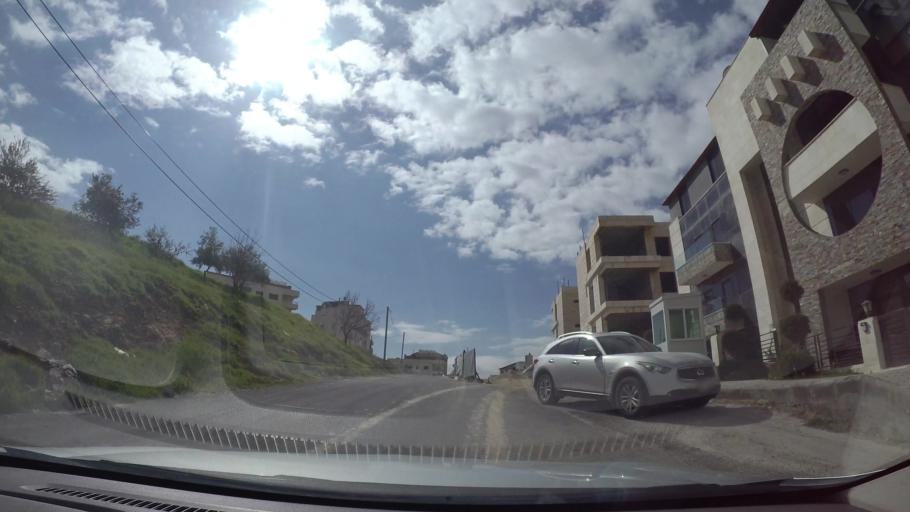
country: JO
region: Amman
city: Al Jubayhah
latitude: 31.9986
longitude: 35.8324
